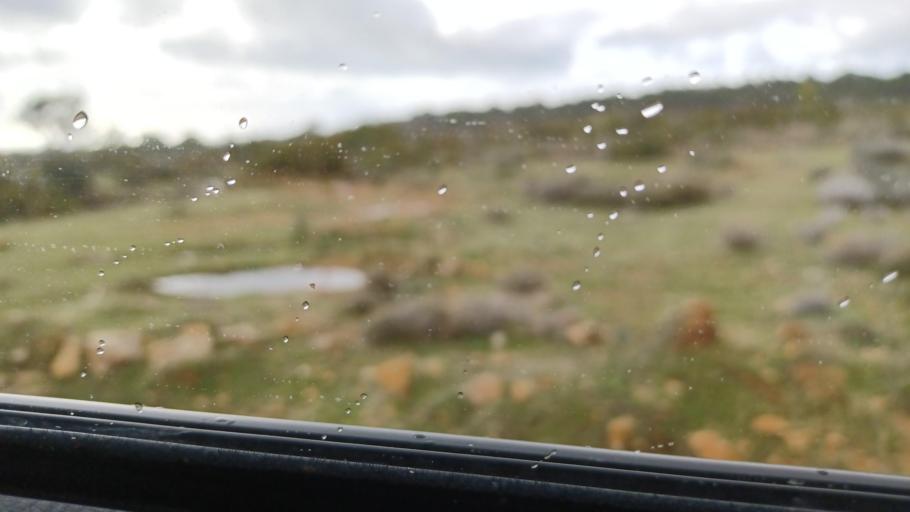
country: CY
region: Limassol
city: Sotira
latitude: 34.7408
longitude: 32.8599
